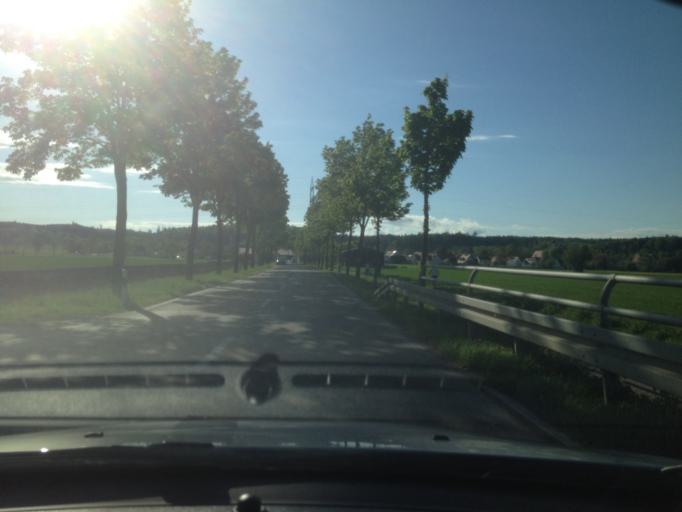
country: DE
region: Bavaria
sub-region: Swabia
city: Bobingen
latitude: 48.3129
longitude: 10.8280
